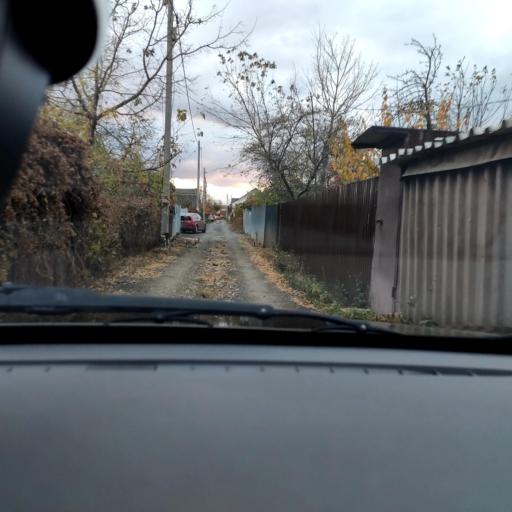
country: RU
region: Samara
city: Tol'yatti
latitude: 53.5407
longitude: 49.4294
